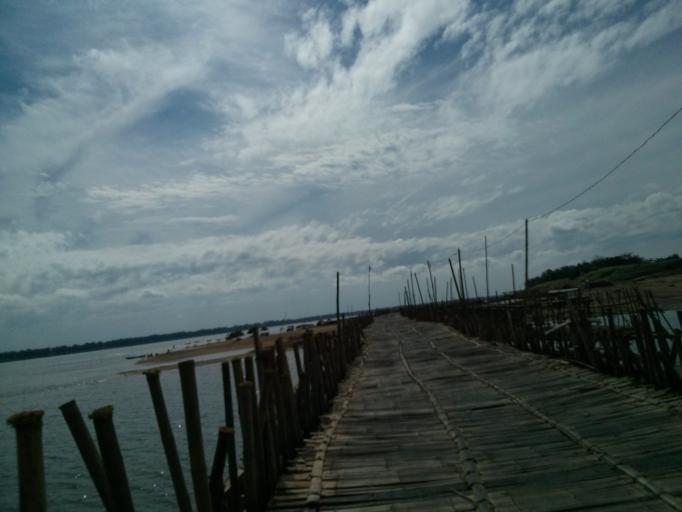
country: KH
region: Kampong Cham
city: Kampong Cham
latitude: 11.9728
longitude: 105.4627
